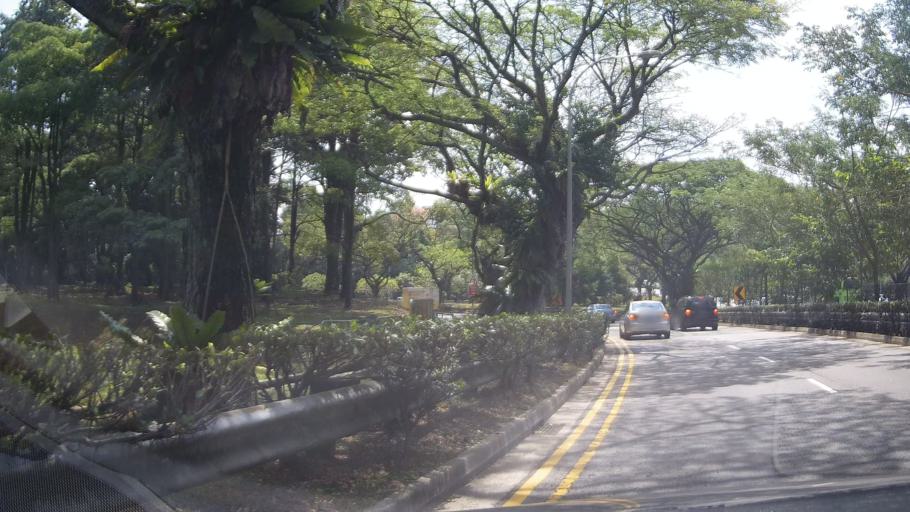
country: SG
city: Singapore
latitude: 1.3329
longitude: 103.7649
